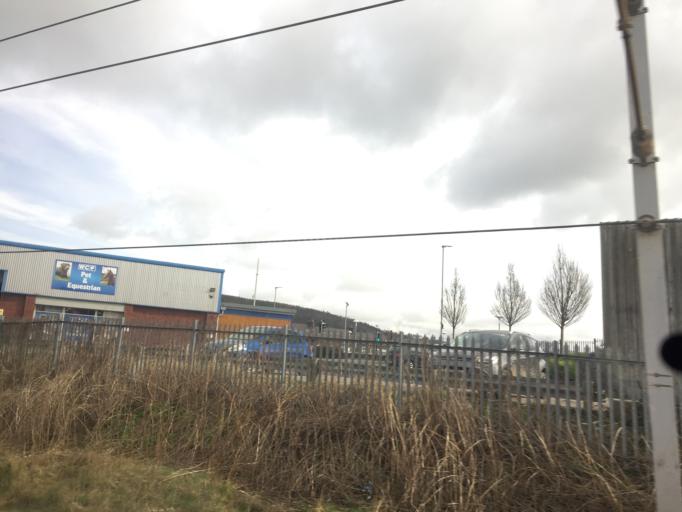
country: GB
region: England
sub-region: Cumbria
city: Penrith
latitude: 54.6637
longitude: -2.7585
